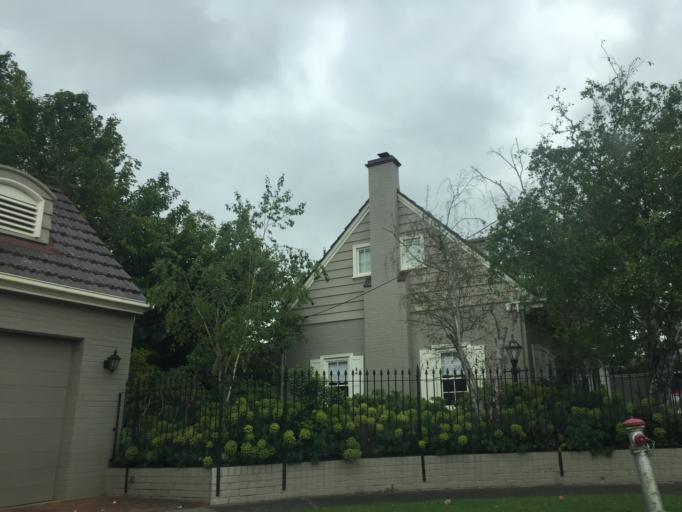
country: AU
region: Victoria
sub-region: Boroondara
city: Hawthorn East
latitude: -37.8140
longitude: 145.0514
